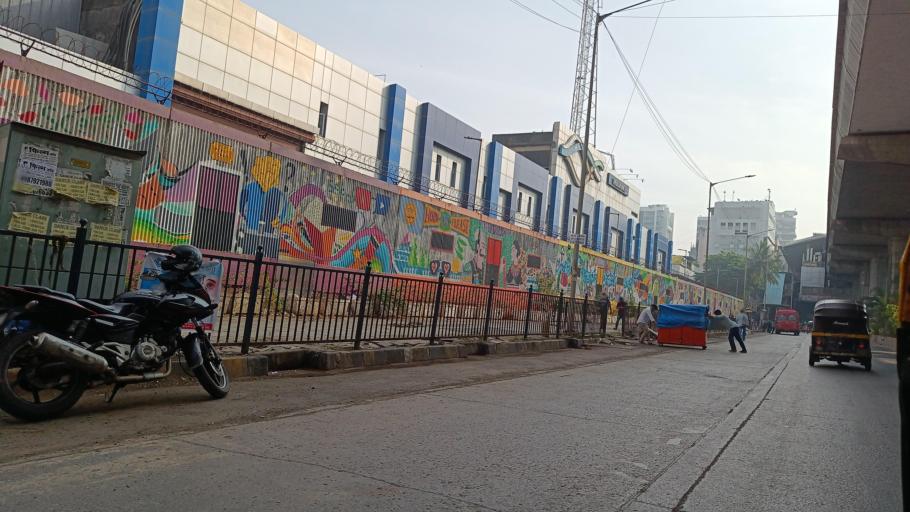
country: IN
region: Maharashtra
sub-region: Mumbai Suburban
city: Powai
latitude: 19.1288
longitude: 72.8281
